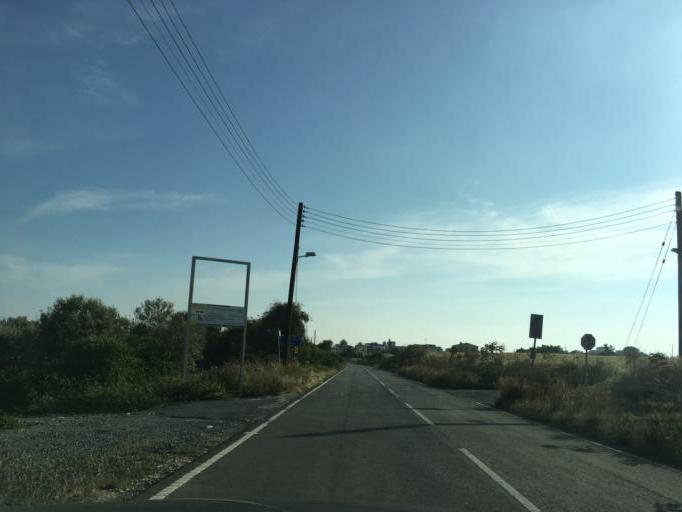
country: CY
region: Larnaka
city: Kofinou
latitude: 34.7602
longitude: 33.4221
